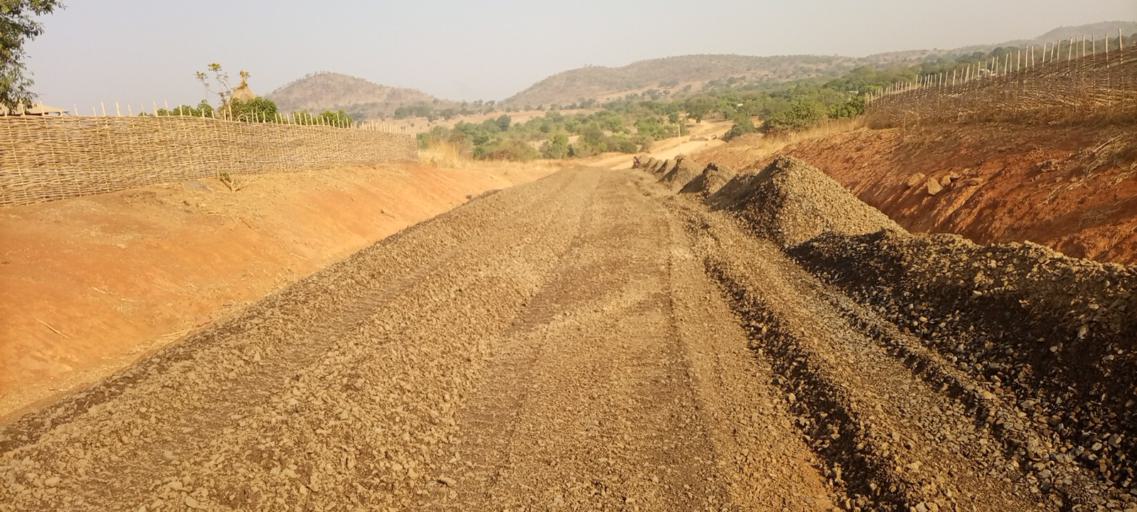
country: ET
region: Oromiya
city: Mendi
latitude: 10.2045
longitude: 35.0905
